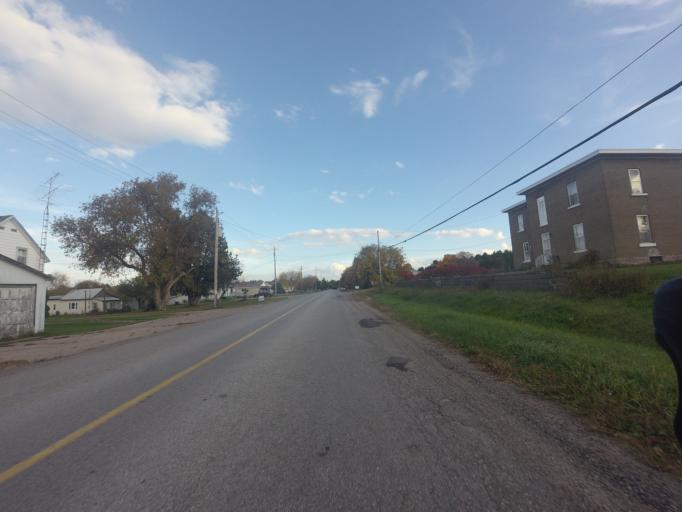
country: CA
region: Ontario
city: Pembroke
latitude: 45.5317
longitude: -77.0902
